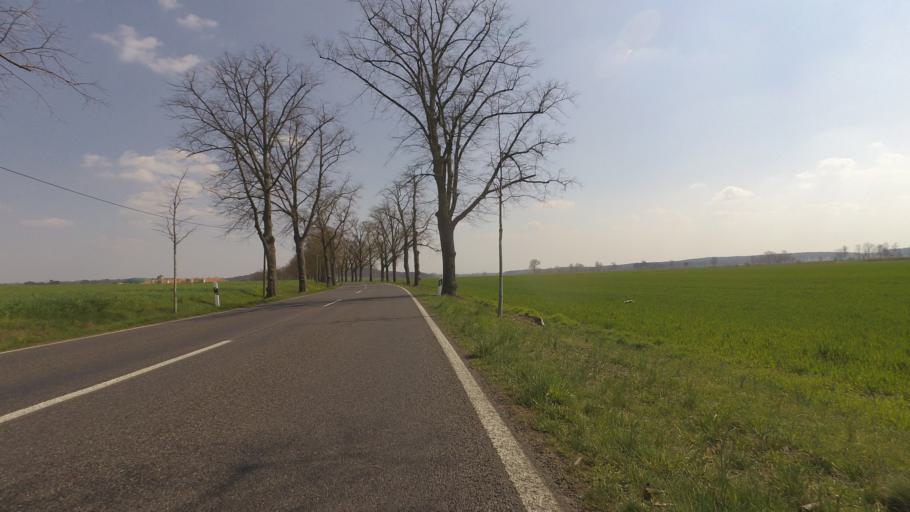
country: DE
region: Brandenburg
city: Mittenwalde
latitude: 52.2715
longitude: 13.4815
